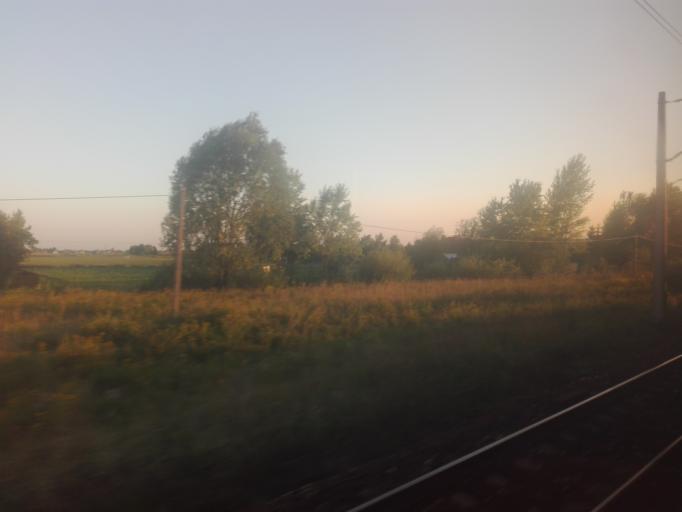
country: PL
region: Masovian Voivodeship
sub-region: Powiat warszawski zachodni
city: Bieniewice
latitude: 52.1862
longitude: 20.5835
